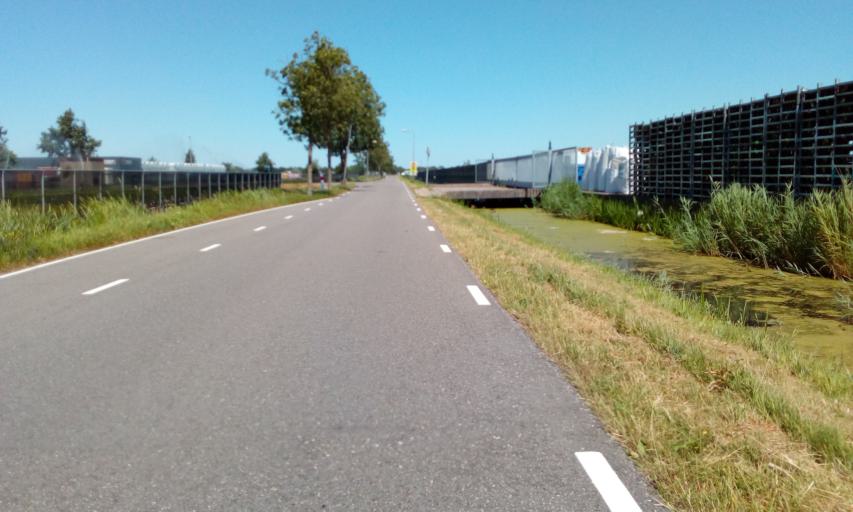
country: NL
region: South Holland
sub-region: Gemeente Boskoop
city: Boskoop
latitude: 52.0946
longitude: 4.6846
